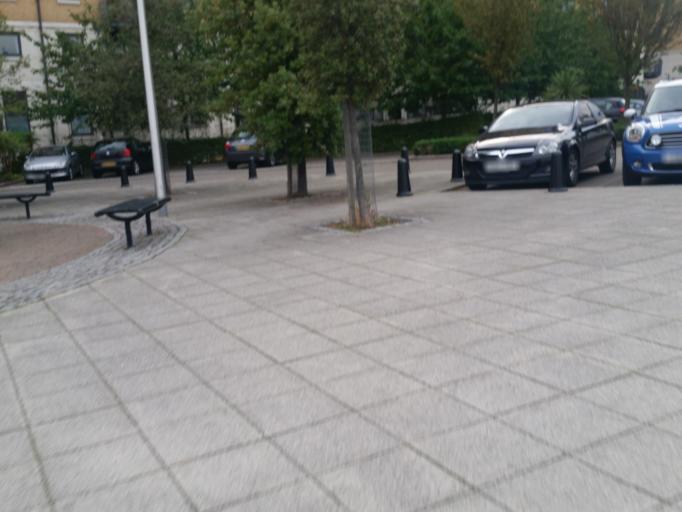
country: GB
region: England
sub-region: Greater London
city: Poplar
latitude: 51.4834
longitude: -0.0190
